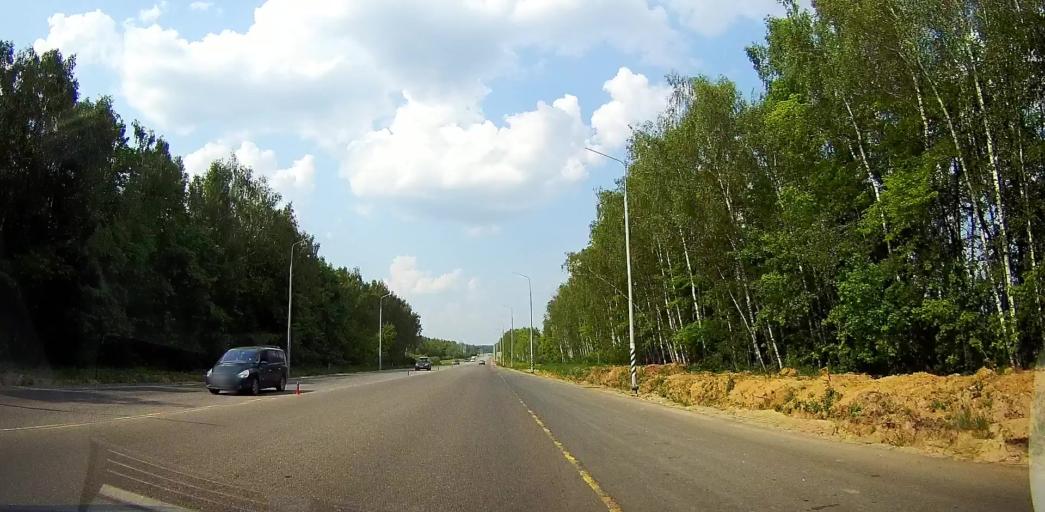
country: RU
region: Moskovskaya
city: Mikhnevo
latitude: 55.0600
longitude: 37.9547
